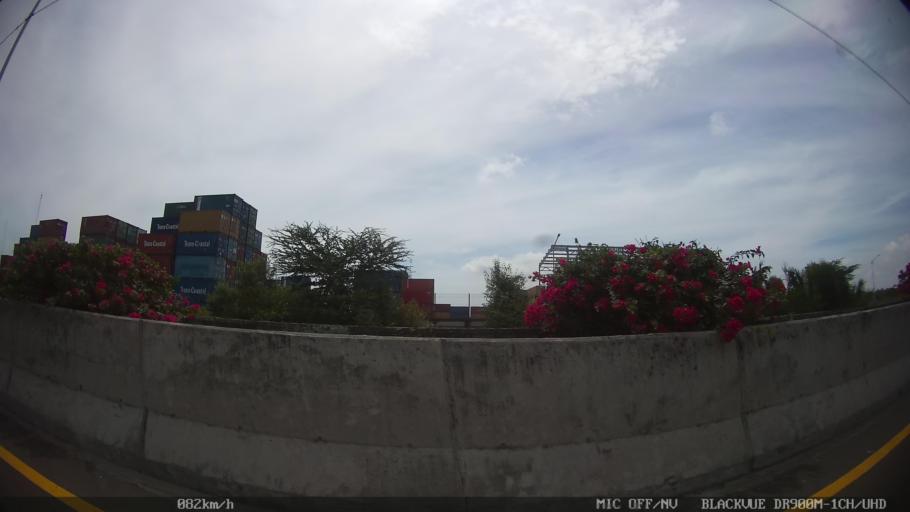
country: ID
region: North Sumatra
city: Belawan
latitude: 3.7660
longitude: 98.6839
